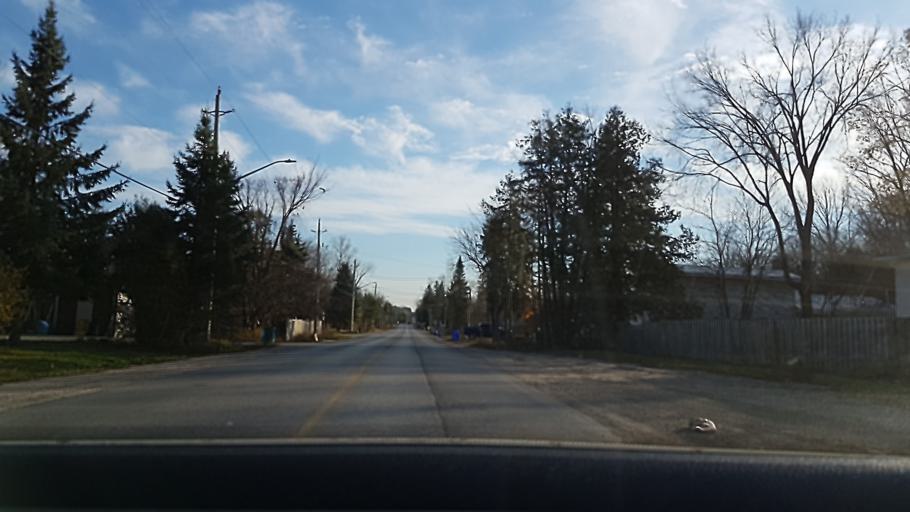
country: CA
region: Ontario
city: Innisfil
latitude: 44.3412
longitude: -79.5460
